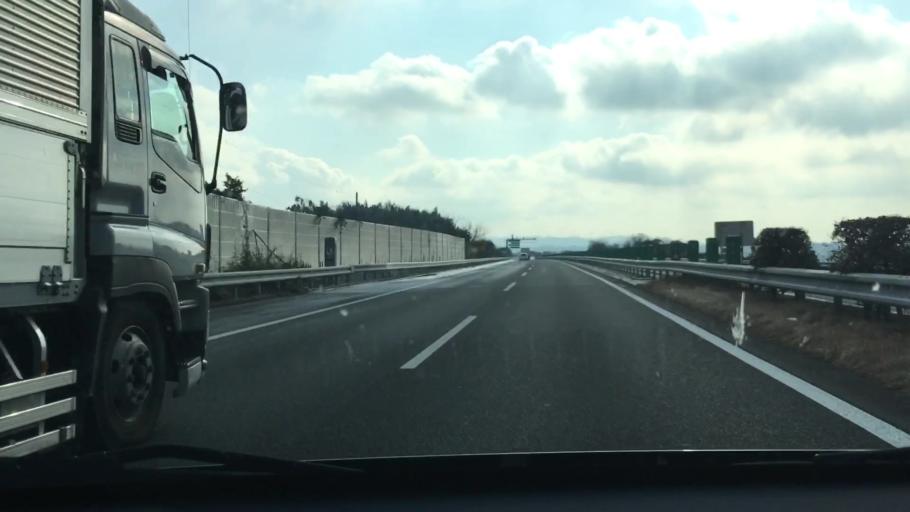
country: JP
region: Kumamoto
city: Uto
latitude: 32.7235
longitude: 130.7714
